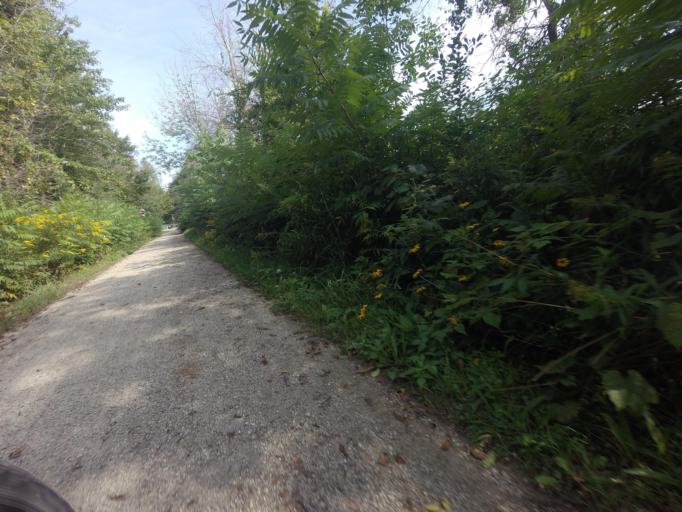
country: CA
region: Ontario
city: Waterloo
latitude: 43.5849
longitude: -80.4218
